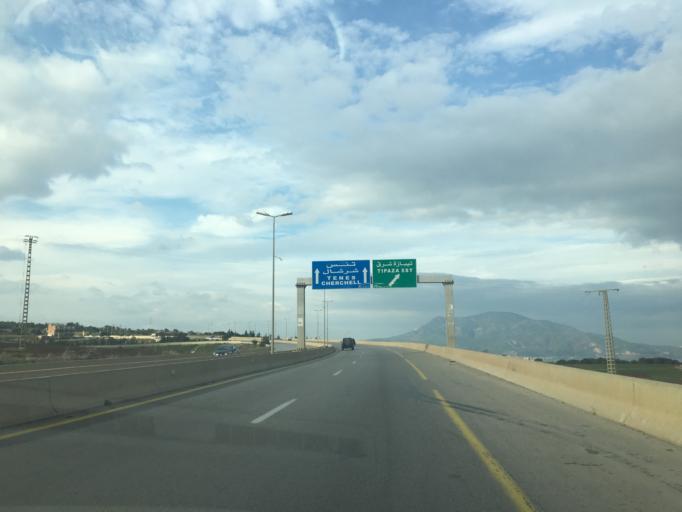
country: DZ
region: Tipaza
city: Tipasa
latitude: 36.5768
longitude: 2.5058
